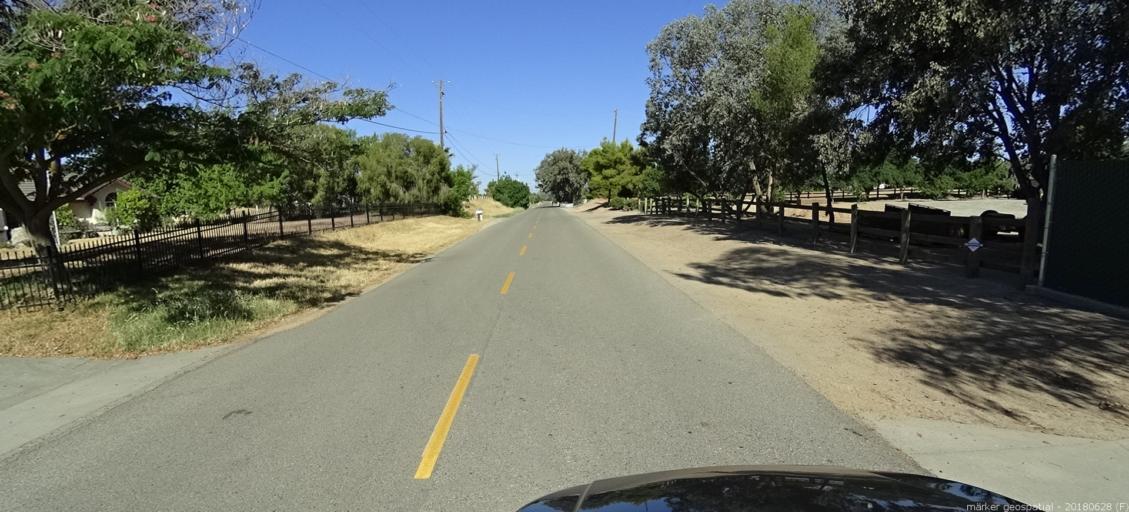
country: US
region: California
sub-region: Madera County
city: Bonadelle Ranchos-Madera Ranchos
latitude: 36.9782
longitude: -119.8818
